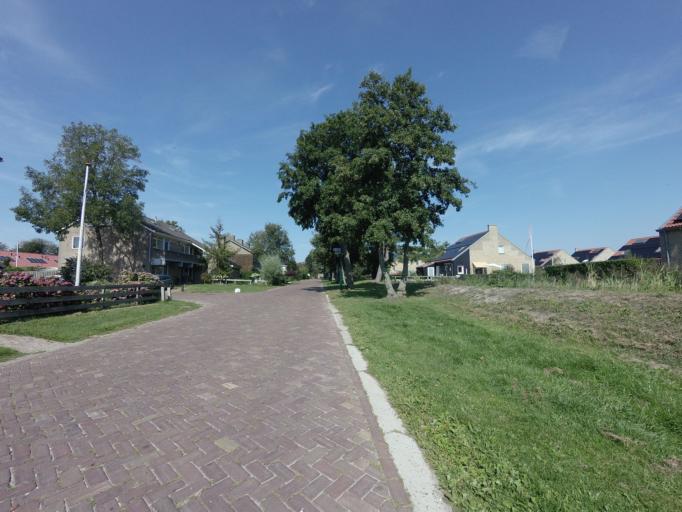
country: NL
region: Friesland
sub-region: Gemeente Schiermonnikoog
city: Schiermonnikoog
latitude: 53.4781
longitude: 6.1663
